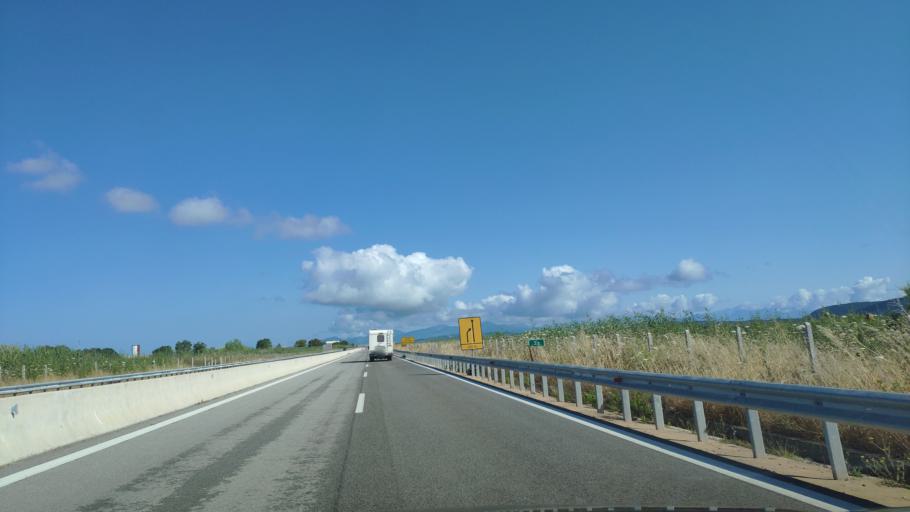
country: GR
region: Epirus
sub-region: Nomos Prevezis
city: Preveza
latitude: 38.9213
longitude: 20.7883
